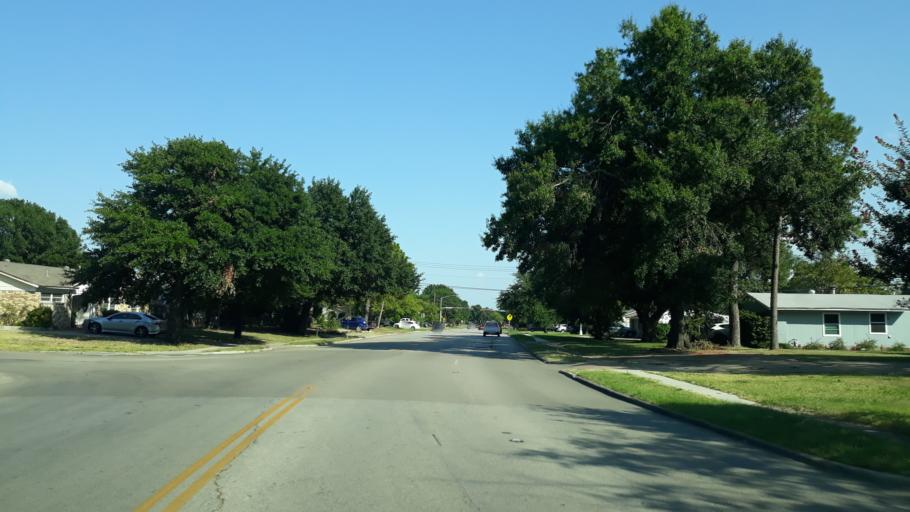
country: US
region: Texas
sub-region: Dallas County
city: Irving
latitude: 32.8448
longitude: -96.9837
